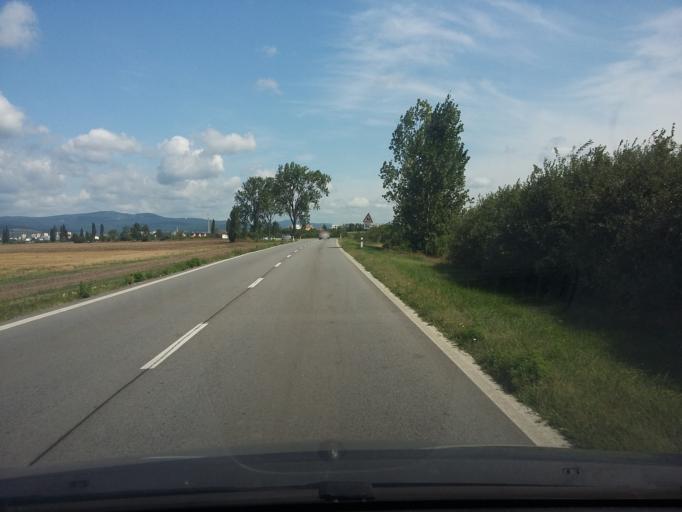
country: SK
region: Bratislavsky
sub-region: Okres Pezinok
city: Pezinok
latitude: 48.2479
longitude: 17.2612
